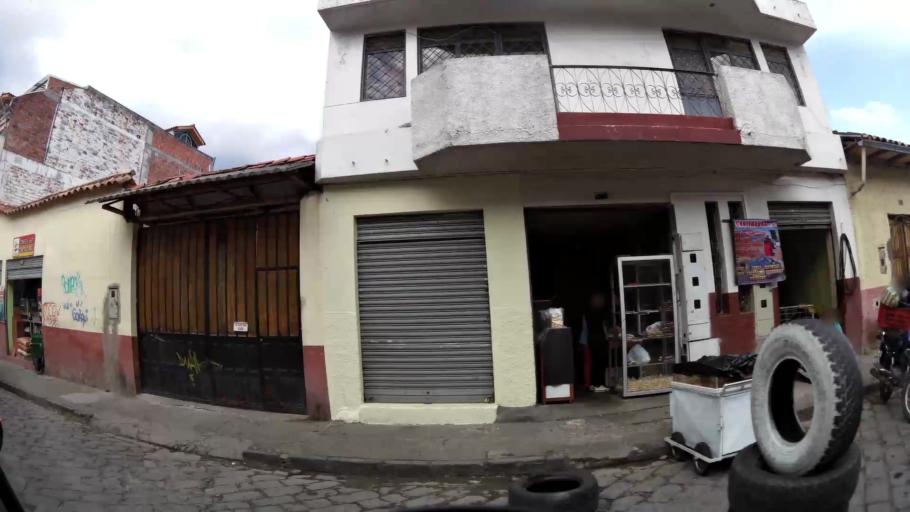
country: EC
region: Azuay
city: Cuenca
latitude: -2.8943
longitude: -79.0117
